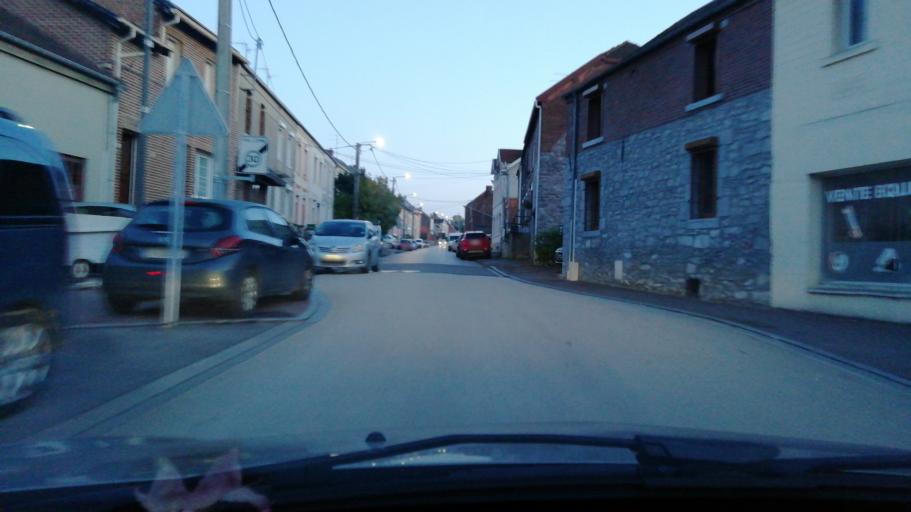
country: FR
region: Nord-Pas-de-Calais
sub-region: Departement du Nord
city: Marpent
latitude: 50.2916
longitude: 4.0811
